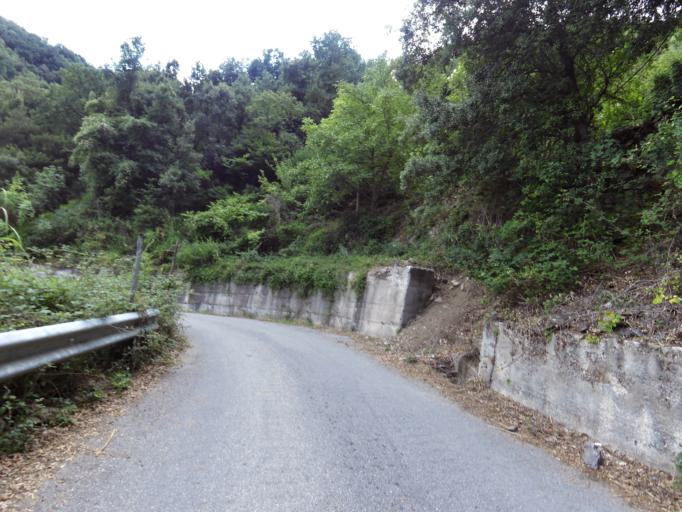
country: IT
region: Calabria
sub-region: Provincia di Reggio Calabria
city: Bivongi
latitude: 38.4849
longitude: 16.4289
